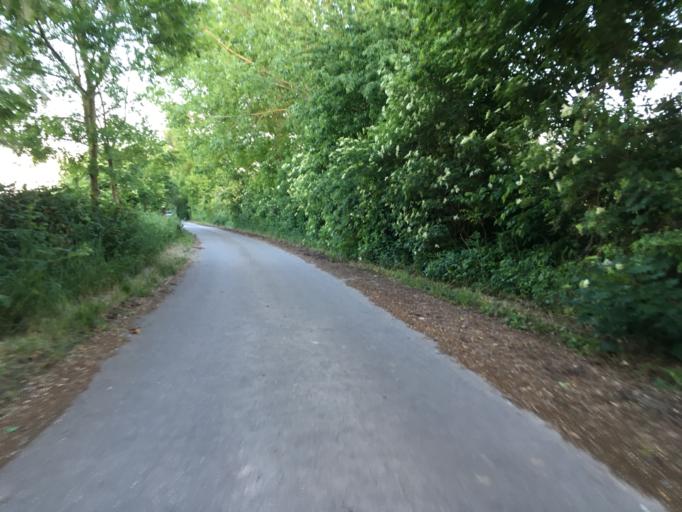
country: DE
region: Baden-Wuerttemberg
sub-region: Regierungsbezirk Stuttgart
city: Lauffen am Neckar
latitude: 49.0983
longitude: 9.1523
